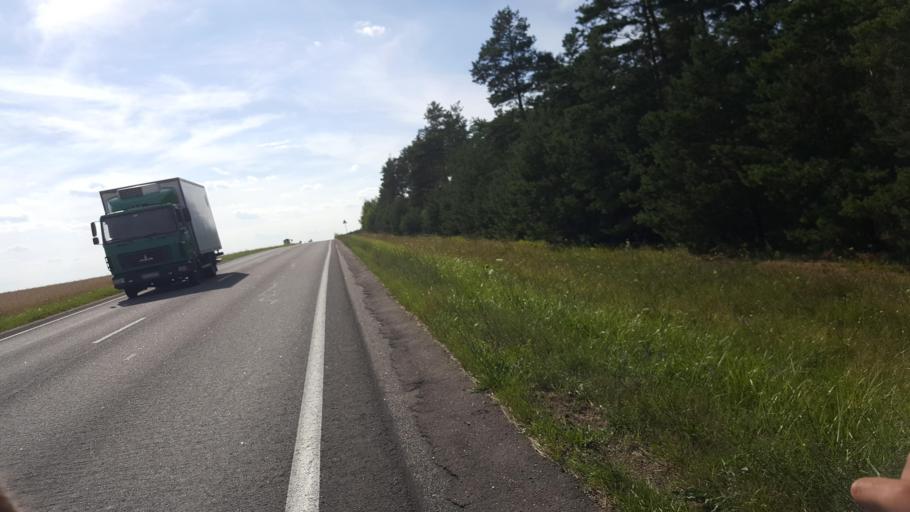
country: BY
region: Brest
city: Kamyanyets
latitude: 52.3928
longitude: 23.9584
